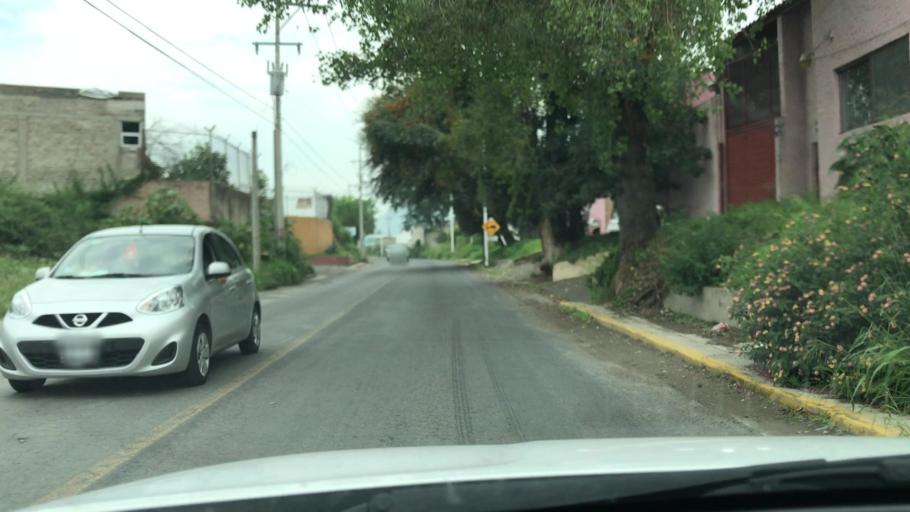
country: MX
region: Jalisco
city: Nicolas R Casillas
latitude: 20.5475
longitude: -103.4752
